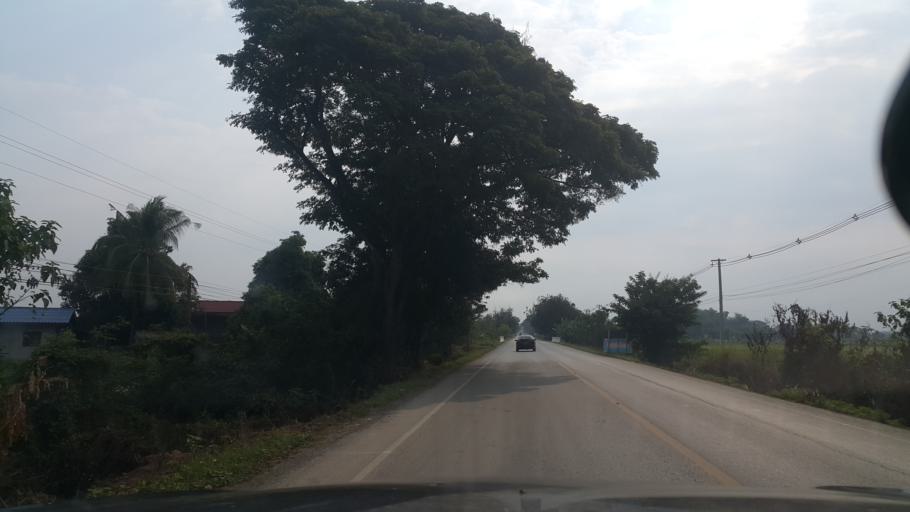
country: TH
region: Sukhothai
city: Si Samrong
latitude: 17.1812
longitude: 99.8364
